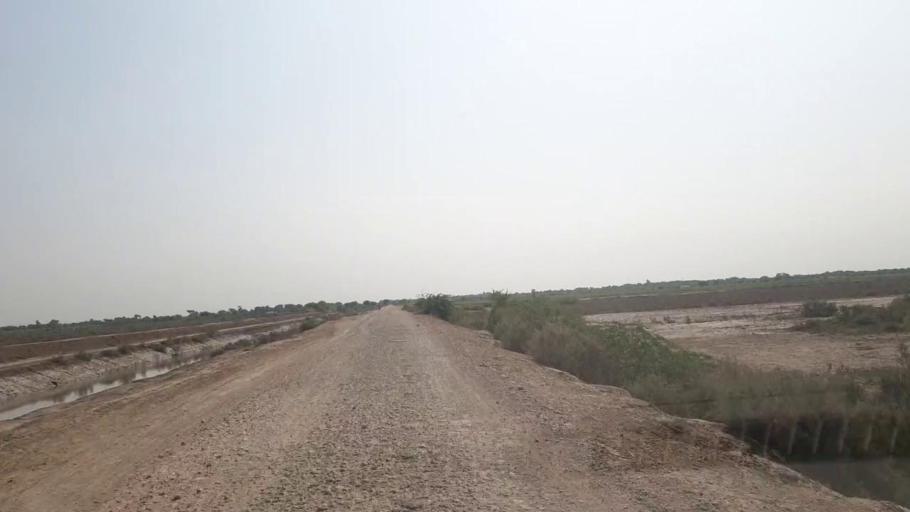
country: PK
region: Sindh
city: Kadhan
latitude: 24.4703
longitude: 68.9041
